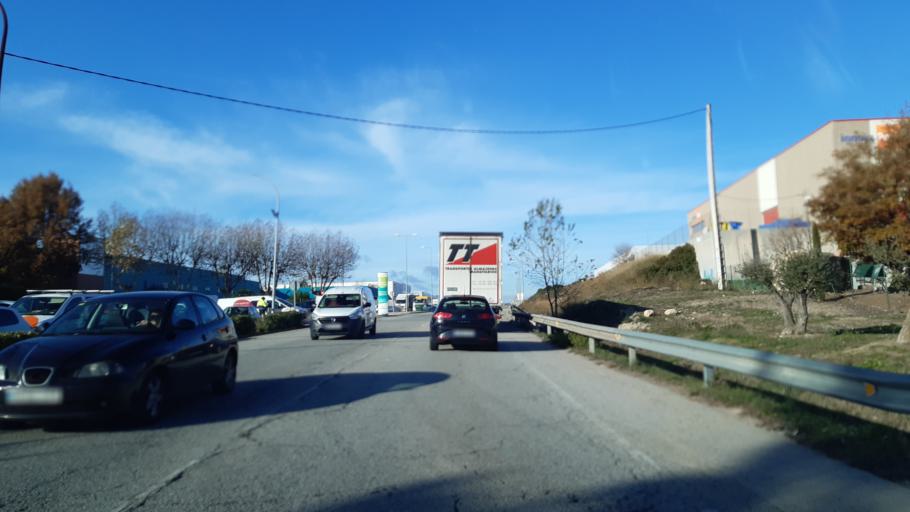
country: ES
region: Catalonia
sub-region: Provincia de Barcelona
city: Vilanova del Cami
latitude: 41.5765
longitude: 1.6614
